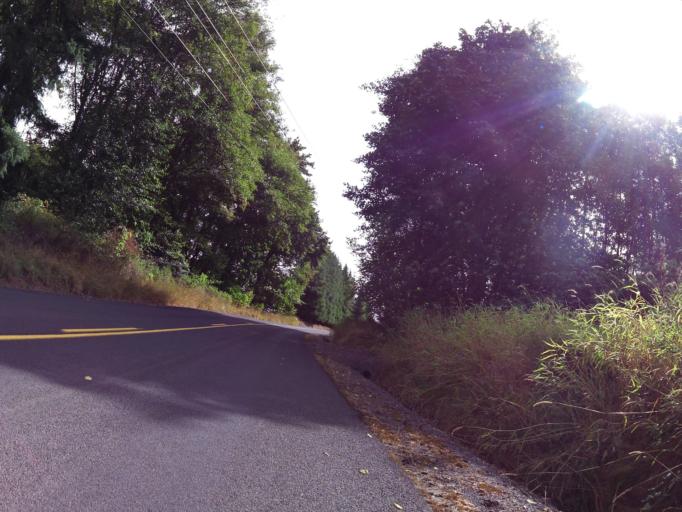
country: US
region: Washington
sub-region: Cowlitz County
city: Castle Rock
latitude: 46.3175
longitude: -122.9246
